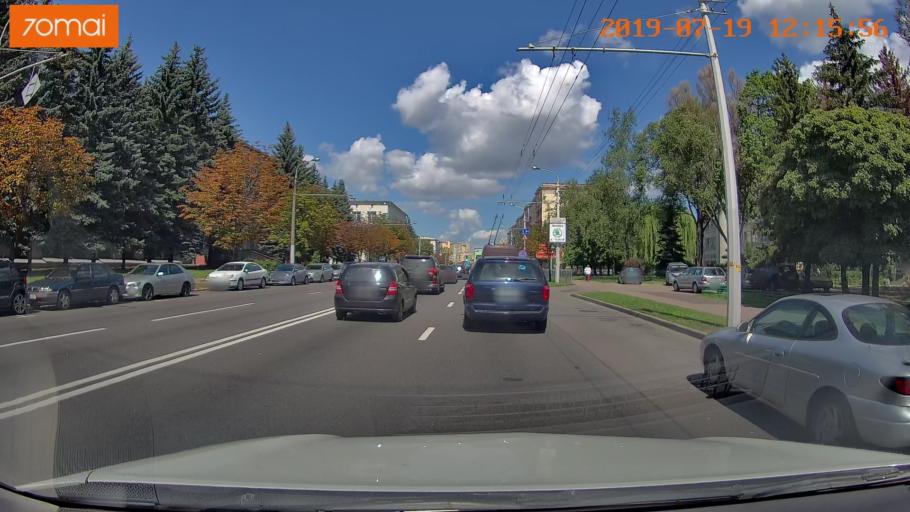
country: BY
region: Minsk
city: Minsk
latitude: 53.9196
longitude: 27.6029
